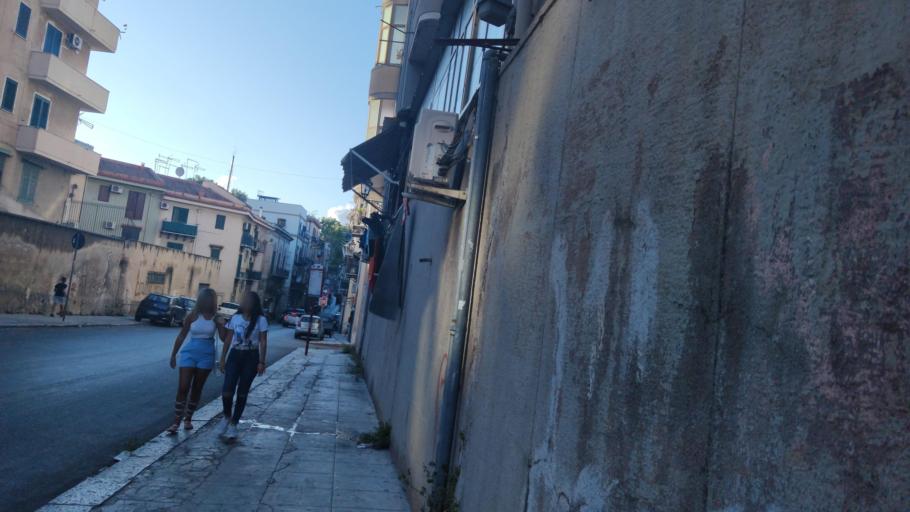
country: IT
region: Sicily
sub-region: Palermo
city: Palermo
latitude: 38.1101
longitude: 13.3562
